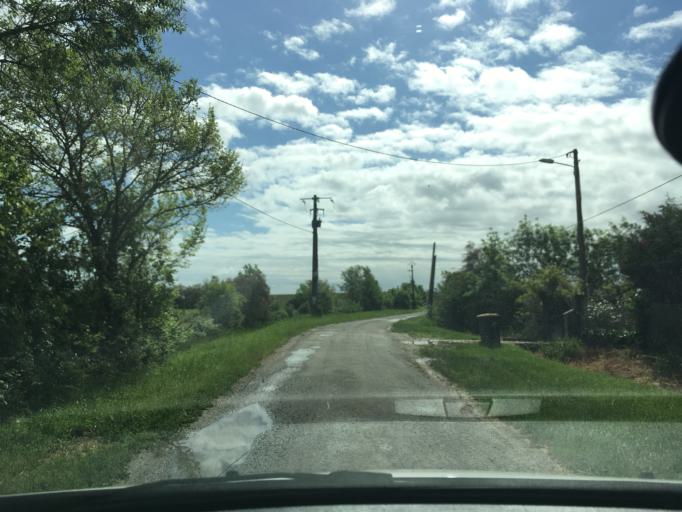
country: FR
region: Aquitaine
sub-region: Departement de la Gironde
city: Saint-Estephe
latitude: 45.3239
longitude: -0.7992
